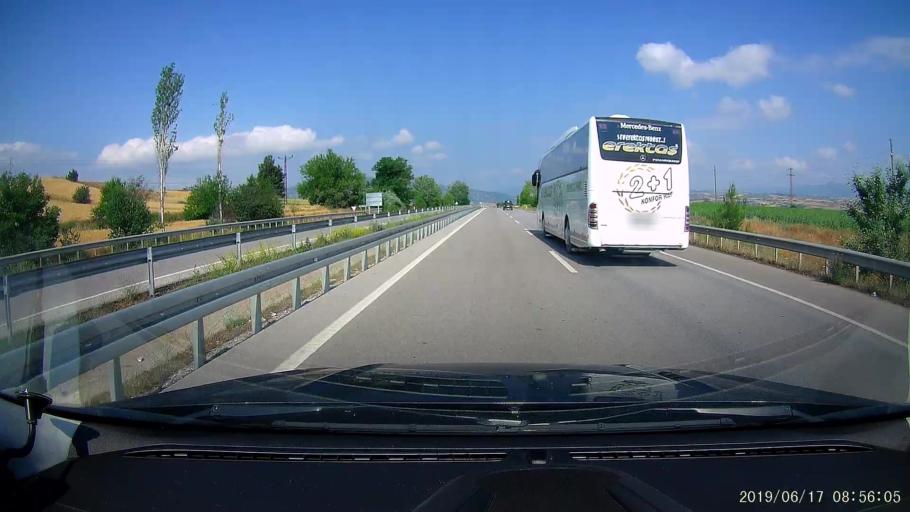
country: TR
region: Amasya
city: Esencay
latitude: 40.7331
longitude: 36.4300
